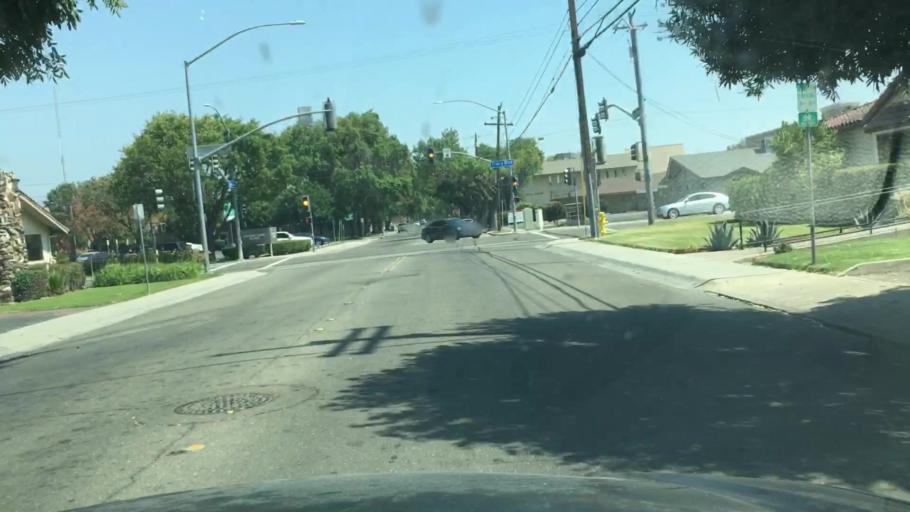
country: US
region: California
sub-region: San Joaquin County
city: Tracy
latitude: 37.7433
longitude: -121.4356
